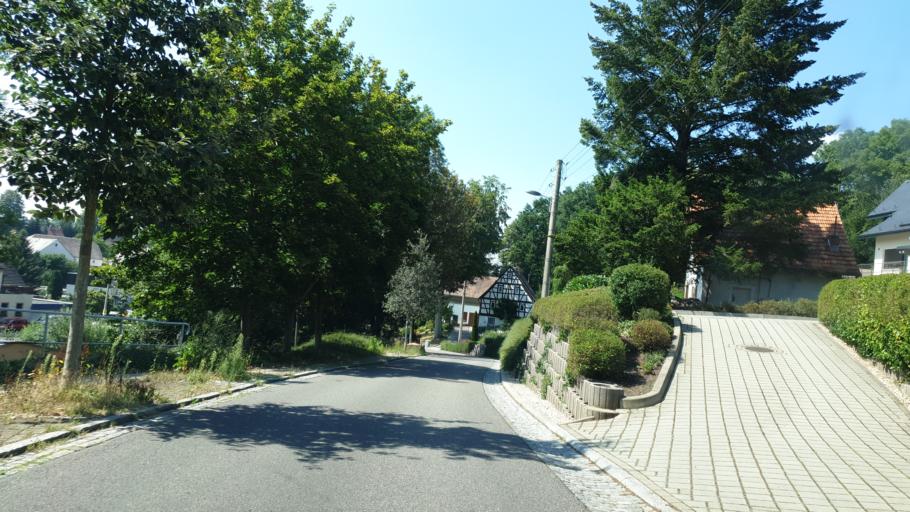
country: DE
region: Saxony
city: Gersdorf
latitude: 50.7510
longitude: 12.7128
